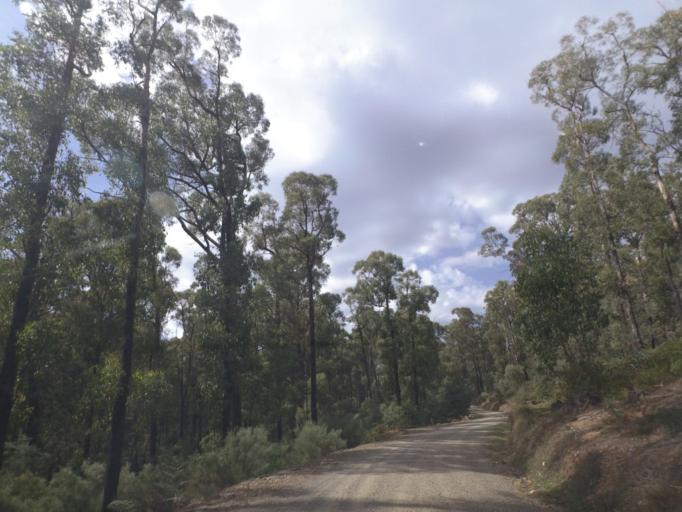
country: AU
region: Victoria
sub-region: Yarra Ranges
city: Healesville
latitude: -37.5352
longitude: 145.7073
